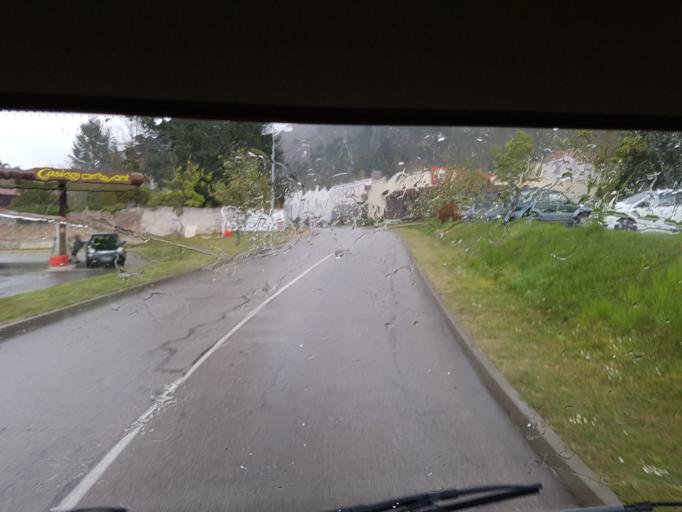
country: FR
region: Auvergne
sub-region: Departement de la Haute-Loire
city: Aurec-sur-Loire
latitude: 45.3713
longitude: 4.2075
